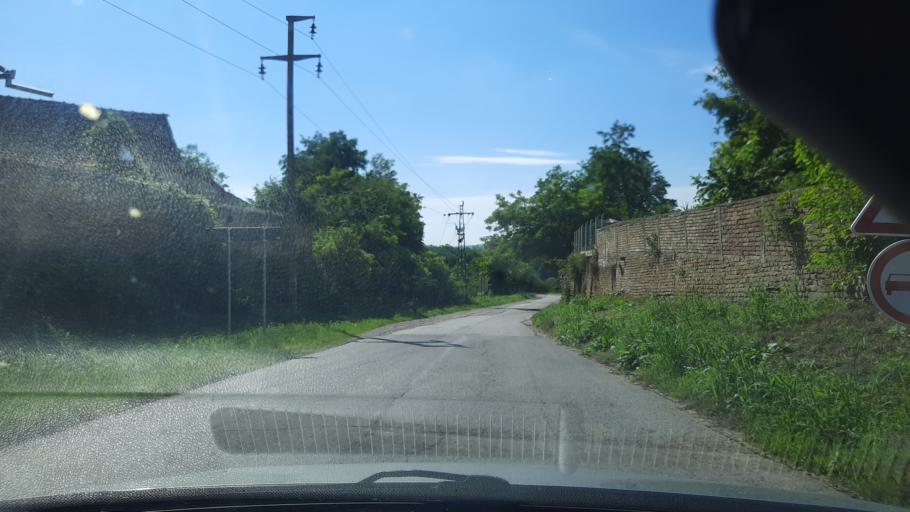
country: RS
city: Cortanovci
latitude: 45.1014
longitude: 19.9916
